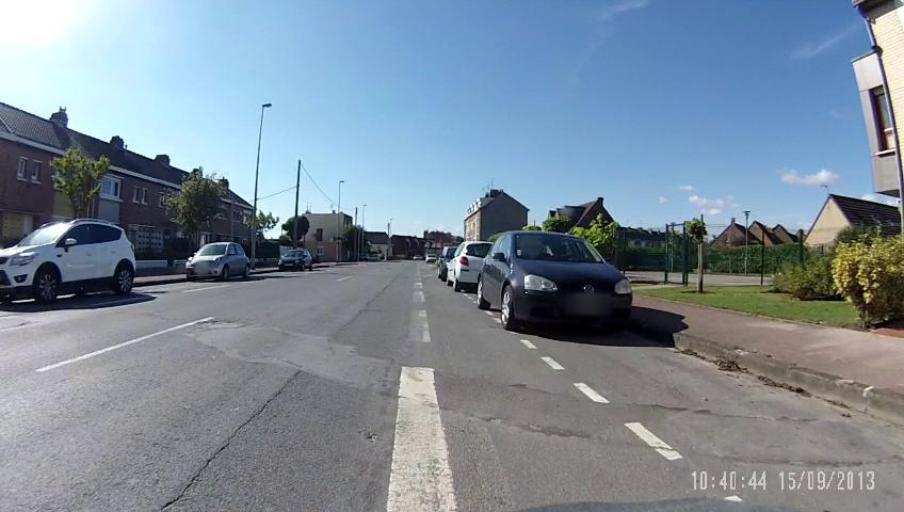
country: FR
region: Nord-Pas-de-Calais
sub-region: Departement du Nord
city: Leffrinckoucke
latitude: 51.0549
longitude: 2.4360
